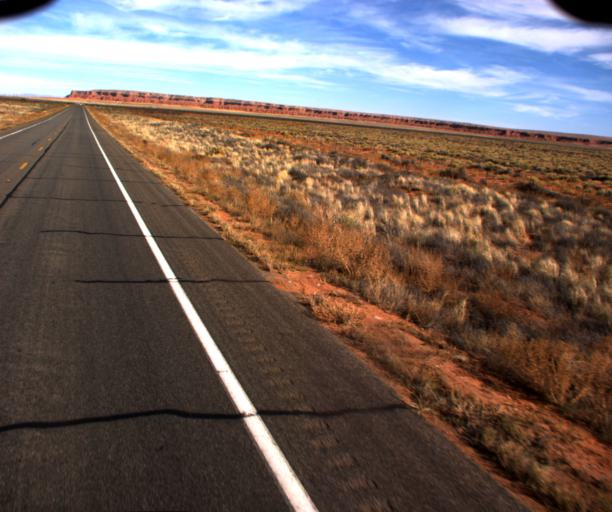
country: US
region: Arizona
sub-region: Navajo County
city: Kayenta
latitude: 36.7792
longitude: -109.9983
